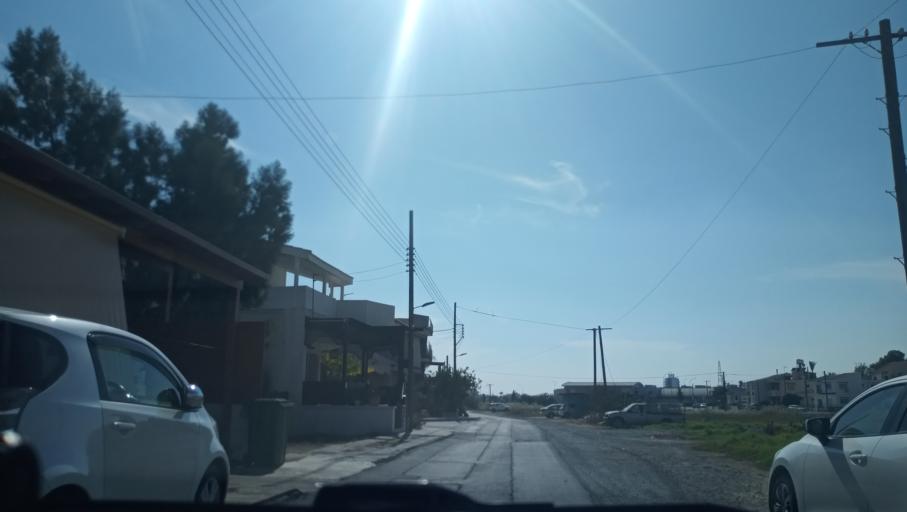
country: CY
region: Larnaka
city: Livadia
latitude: 34.9421
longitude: 33.6290
